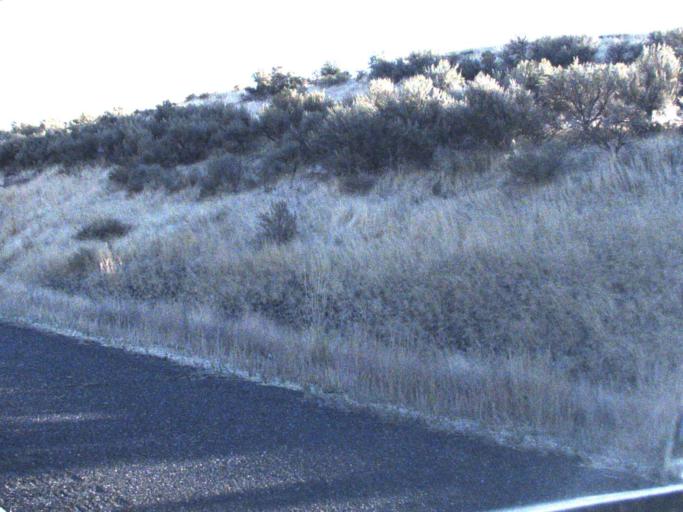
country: US
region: Washington
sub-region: Franklin County
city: Basin City
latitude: 46.4501
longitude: -119.0168
